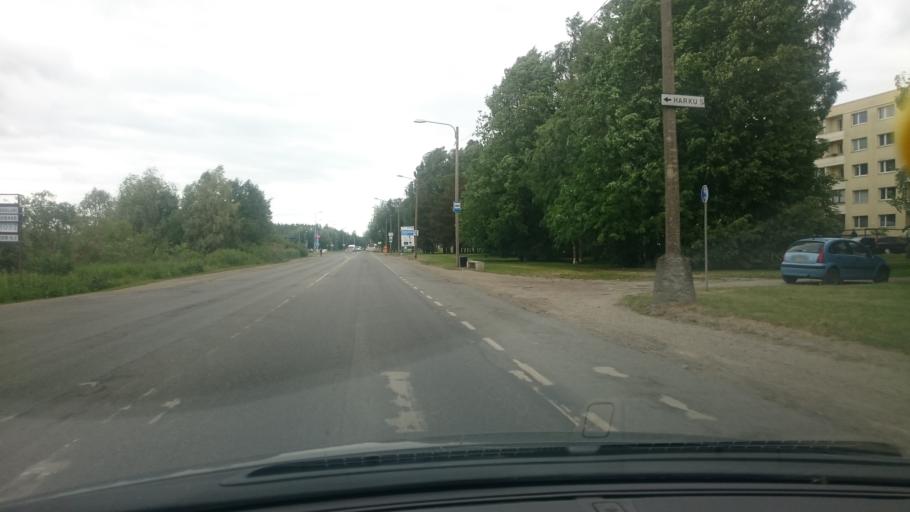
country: EE
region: Harju
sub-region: Saue vald
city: Laagri
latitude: 59.4172
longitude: 24.6367
